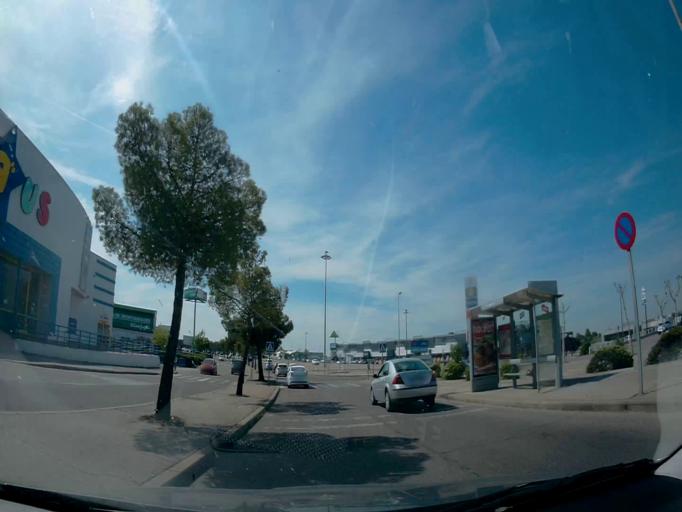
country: ES
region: Madrid
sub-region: Provincia de Madrid
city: Mostoles
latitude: 40.3459
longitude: -3.8525
